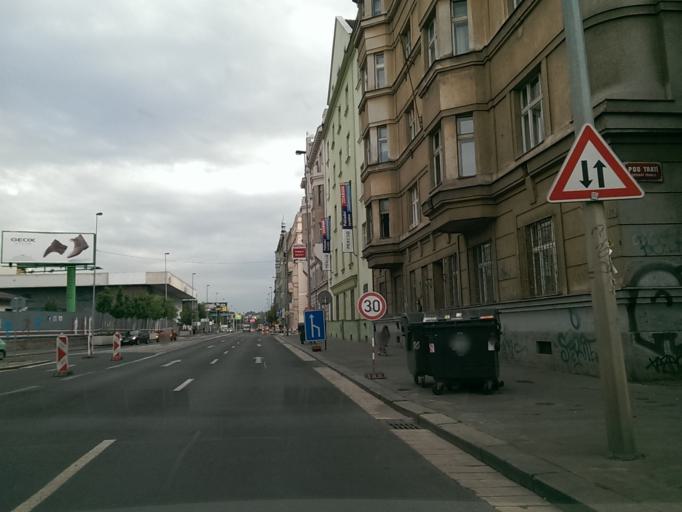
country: CZ
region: Praha
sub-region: Praha 2
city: Vysehrad
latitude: 50.0659
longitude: 14.4100
